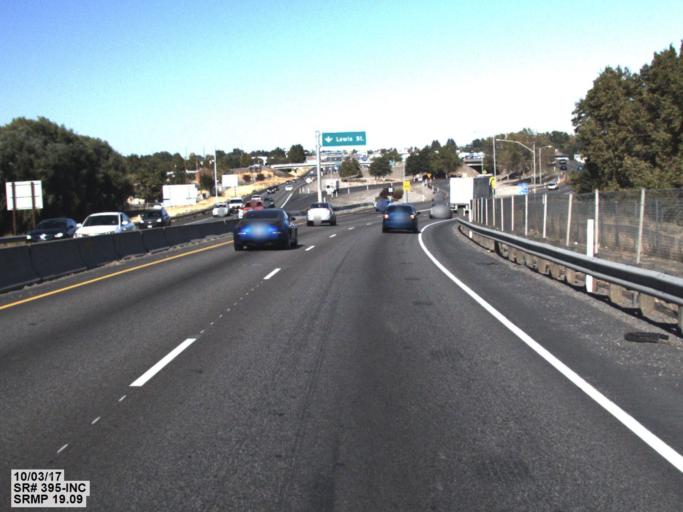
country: US
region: Washington
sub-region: Benton County
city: Kennewick
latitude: 46.2285
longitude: -119.1341
